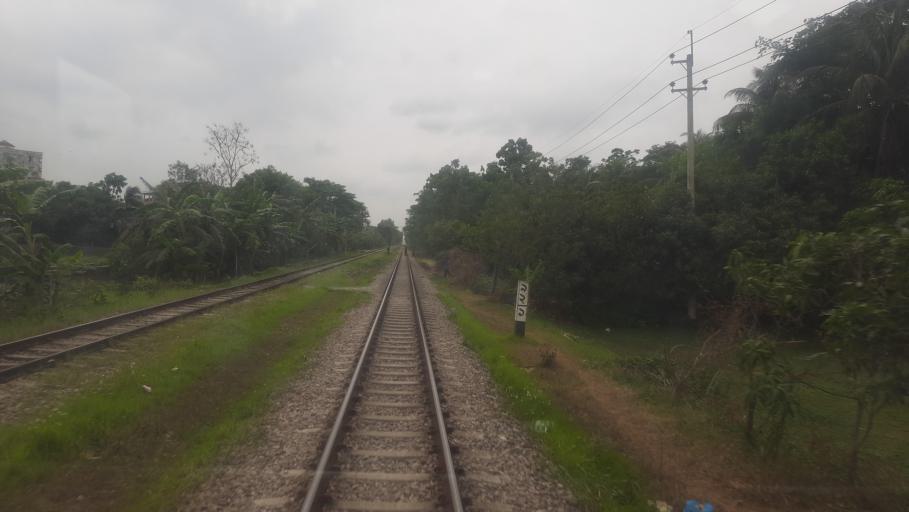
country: BD
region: Chittagong
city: Feni
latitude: 23.0249
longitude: 91.3871
